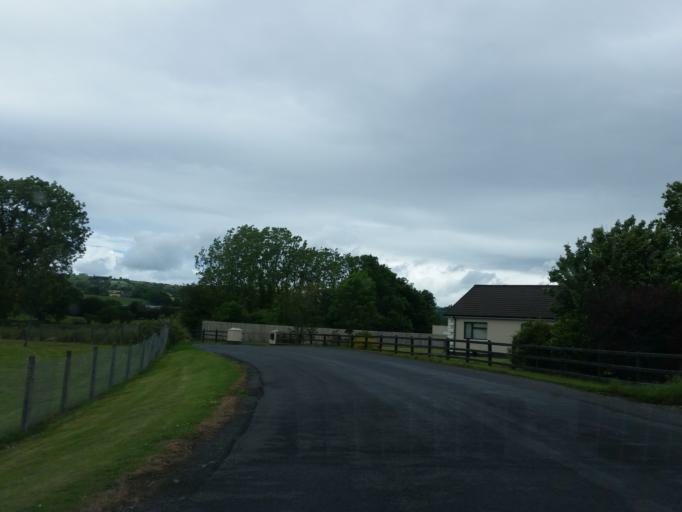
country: IE
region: Ulster
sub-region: County Monaghan
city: Monaghan
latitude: 54.4649
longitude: -7.0277
